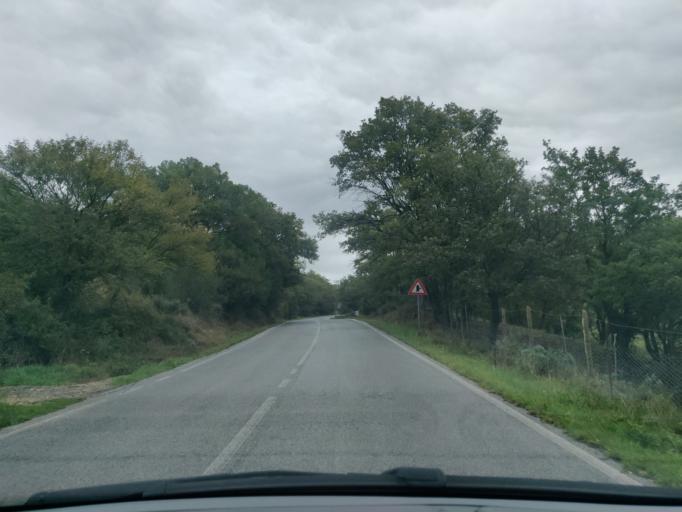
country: IT
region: Latium
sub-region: Citta metropolitana di Roma Capitale
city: Allumiere
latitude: 42.1353
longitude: 11.8704
